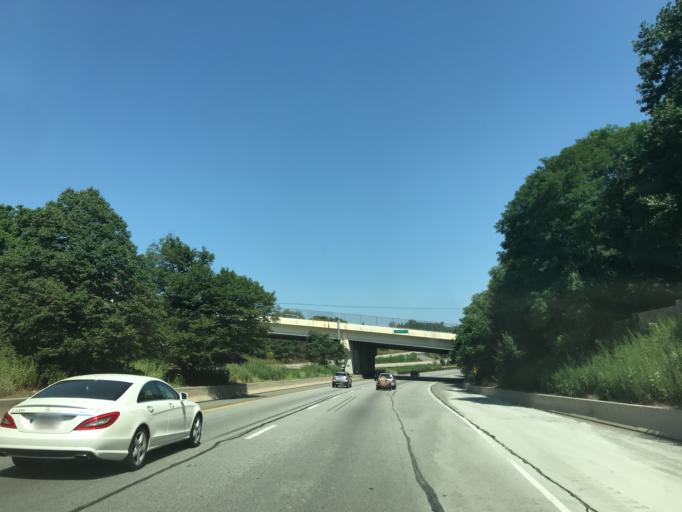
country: US
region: Pennsylvania
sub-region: Delaware County
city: Broomall
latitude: 39.9728
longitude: -75.3397
